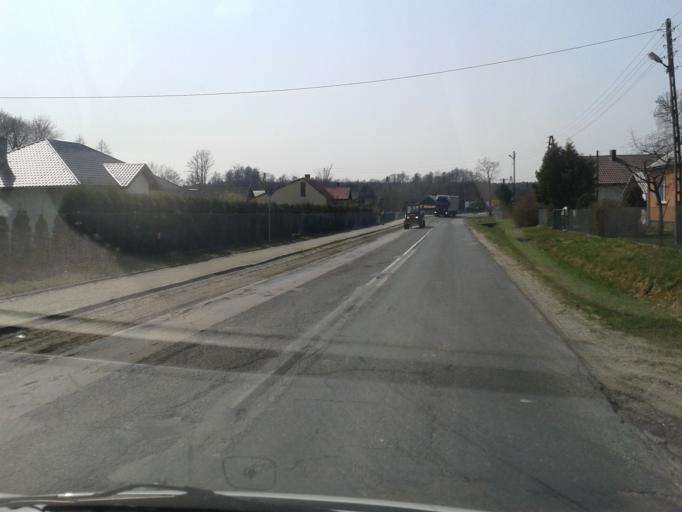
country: PL
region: Subcarpathian Voivodeship
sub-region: Powiat lubaczowski
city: Narol
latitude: 50.3132
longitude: 23.2436
